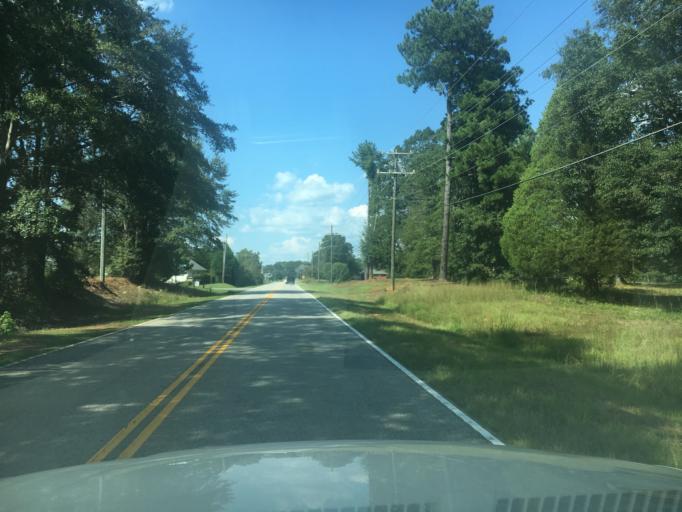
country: US
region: South Carolina
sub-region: Anderson County
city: Pendleton
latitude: 34.5740
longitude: -82.8080
